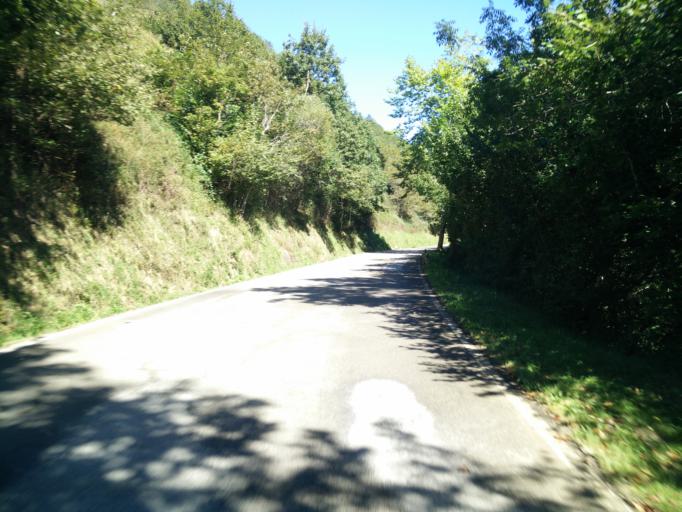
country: ES
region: Cantabria
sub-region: Provincia de Cantabria
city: Ruente
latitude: 43.1483
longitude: -4.2868
